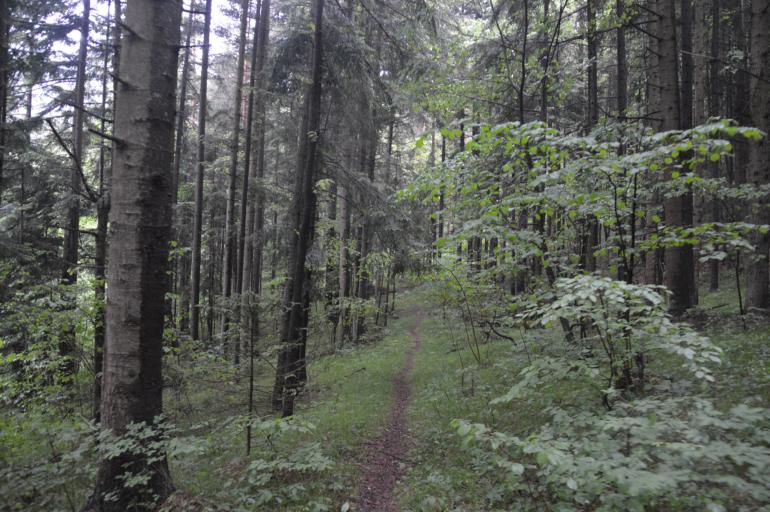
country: SK
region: Presovsky
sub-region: Okres Poprad
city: Poprad
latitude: 48.9608
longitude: 20.3703
